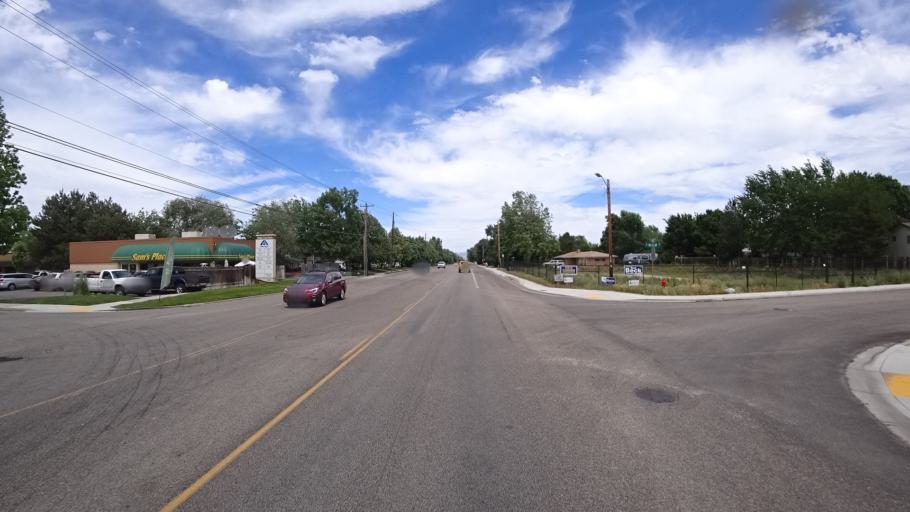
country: US
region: Idaho
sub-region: Ada County
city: Eagle
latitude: 43.6350
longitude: -116.3143
